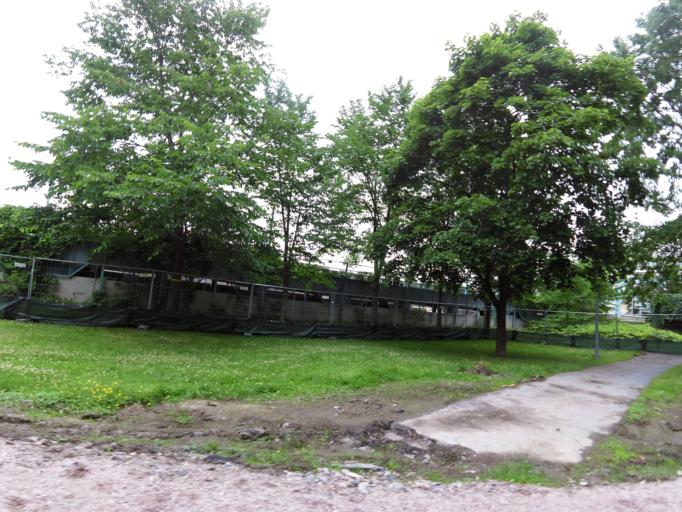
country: FI
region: Uusimaa
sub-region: Helsinki
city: Koukkuniemi
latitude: 60.1692
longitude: 24.7590
